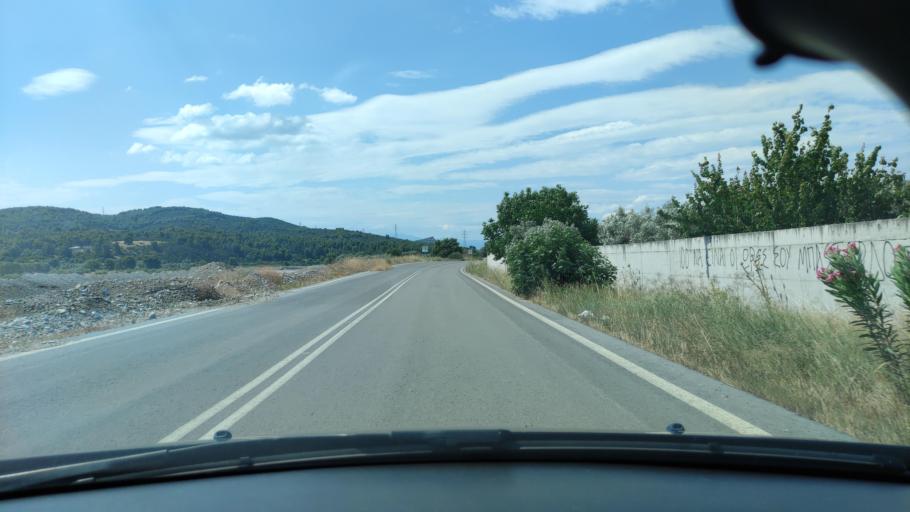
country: GR
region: Central Greece
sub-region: Nomos Evvoias
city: Afration
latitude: 38.4800
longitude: 23.6878
